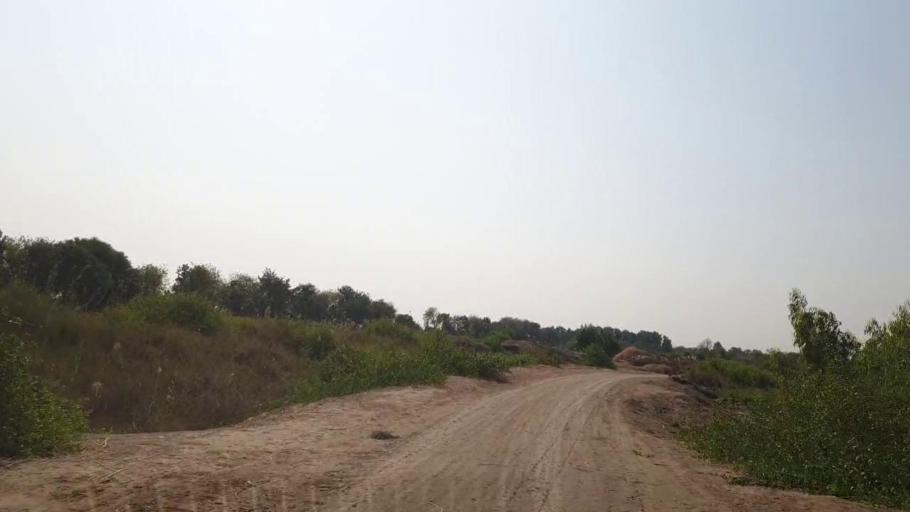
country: PK
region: Sindh
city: Tando Muhammad Khan
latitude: 25.0128
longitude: 68.4185
